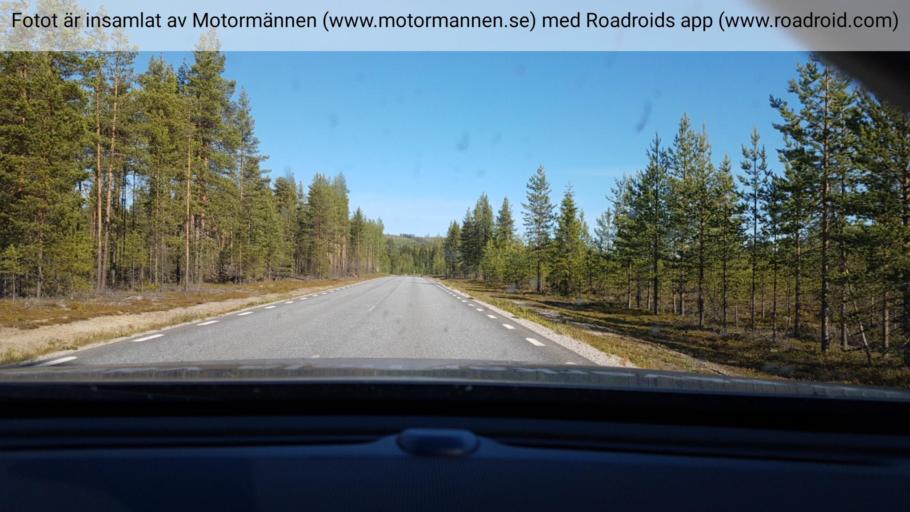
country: SE
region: Vaesterbotten
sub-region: Lycksele Kommun
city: Lycksele
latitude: 64.4347
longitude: 18.9647
